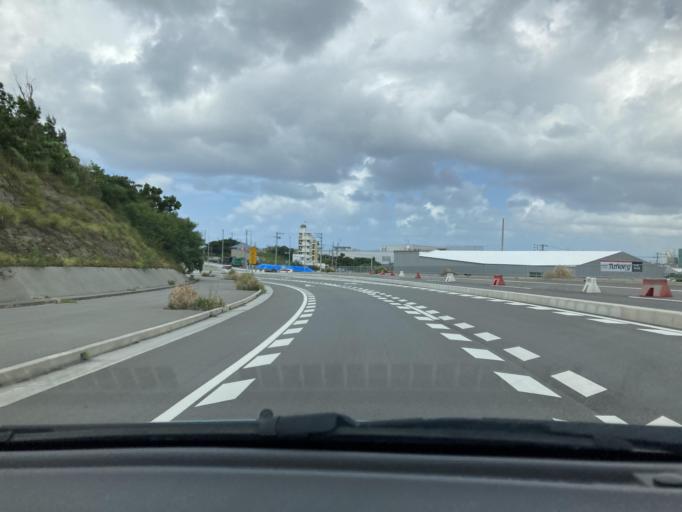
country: JP
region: Okinawa
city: Ginowan
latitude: 26.2679
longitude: 127.7098
